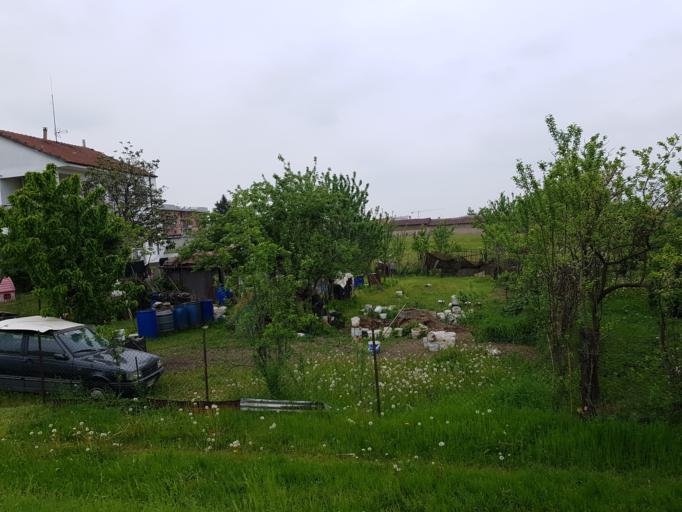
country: IT
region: Piedmont
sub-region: Provincia di Torino
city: Lesna
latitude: 45.0574
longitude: 7.6091
